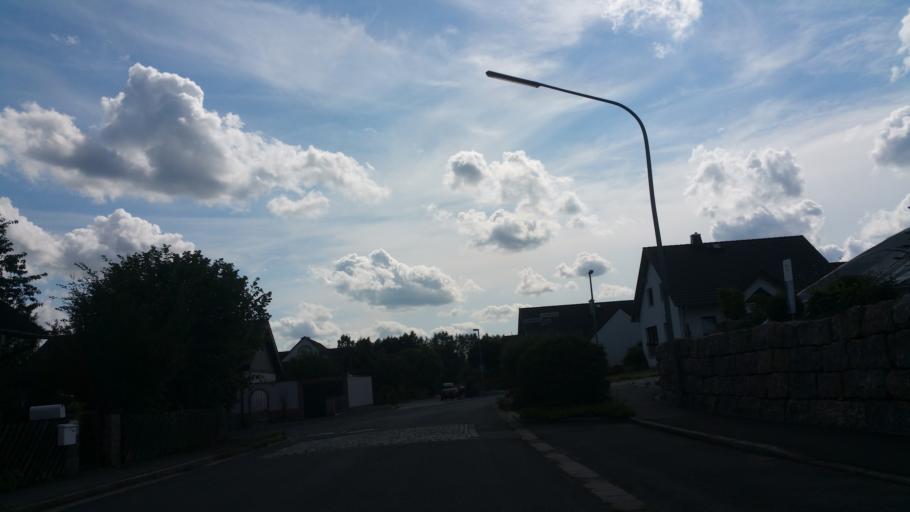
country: DE
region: Bavaria
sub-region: Upper Franconia
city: Oberkotzau
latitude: 50.2528
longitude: 11.9304
